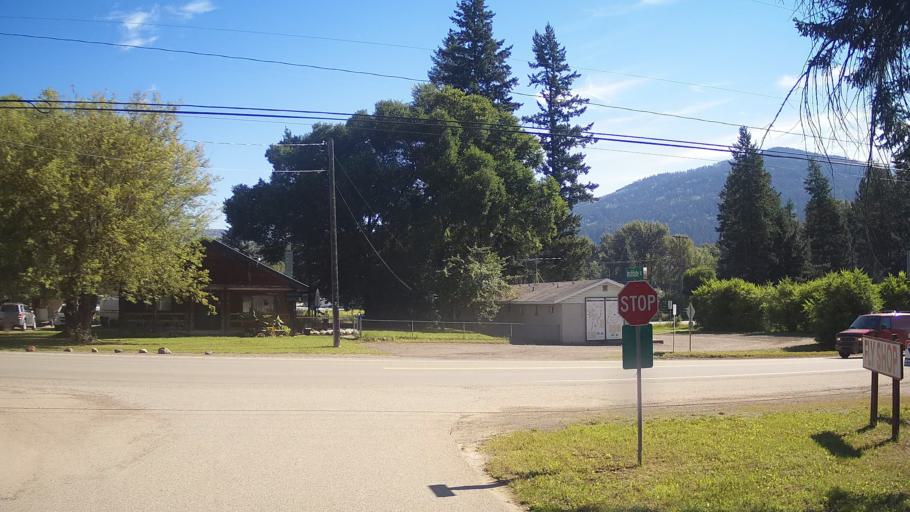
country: CA
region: British Columbia
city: Kamloops
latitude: 51.4242
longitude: -120.2065
